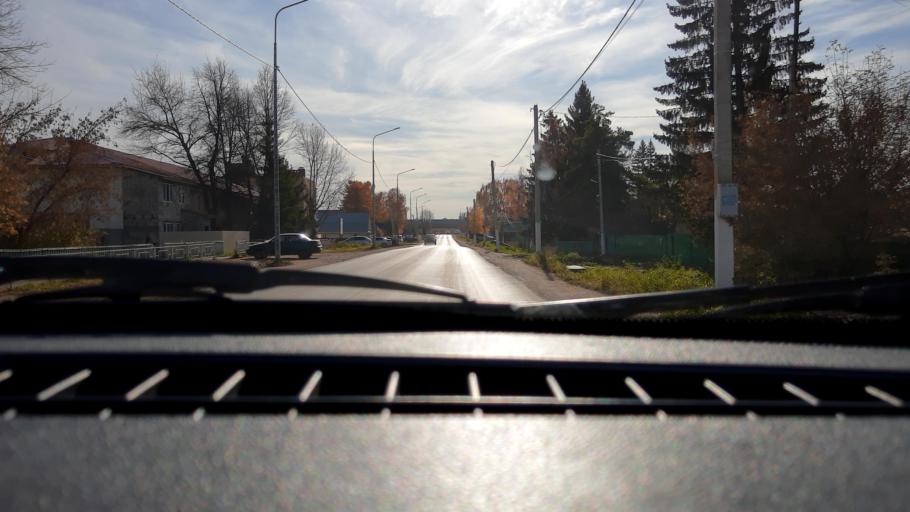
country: RU
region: Bashkortostan
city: Mikhaylovka
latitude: 54.8013
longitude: 55.8919
